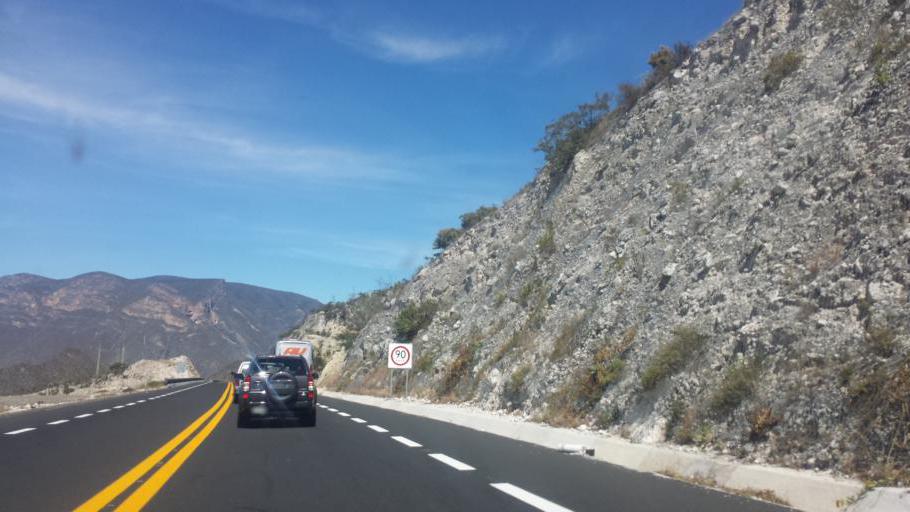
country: MX
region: Puebla
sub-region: San Jose Miahuatlan
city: San Pedro Tetitlan
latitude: 18.0820
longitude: -97.3510
